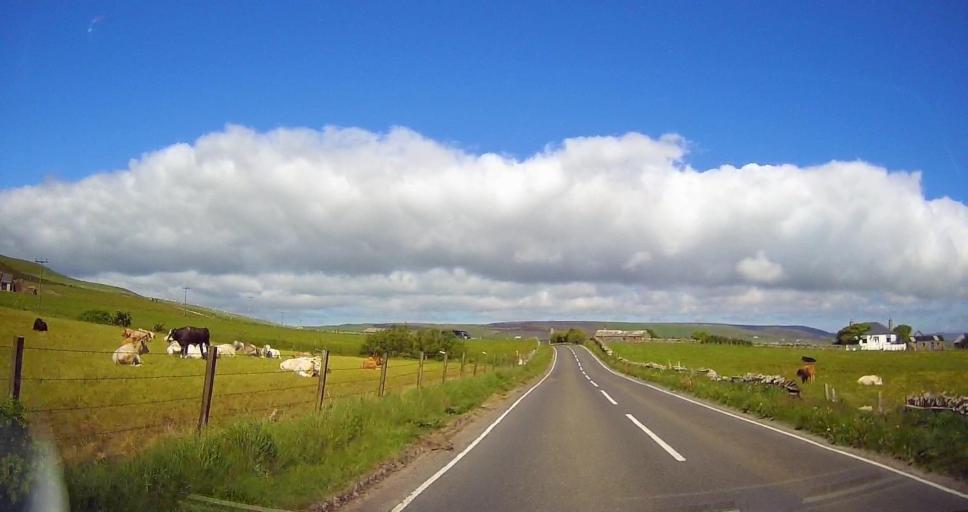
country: GB
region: Scotland
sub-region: Orkney Islands
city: Orkney
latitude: 58.9972
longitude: -3.0984
